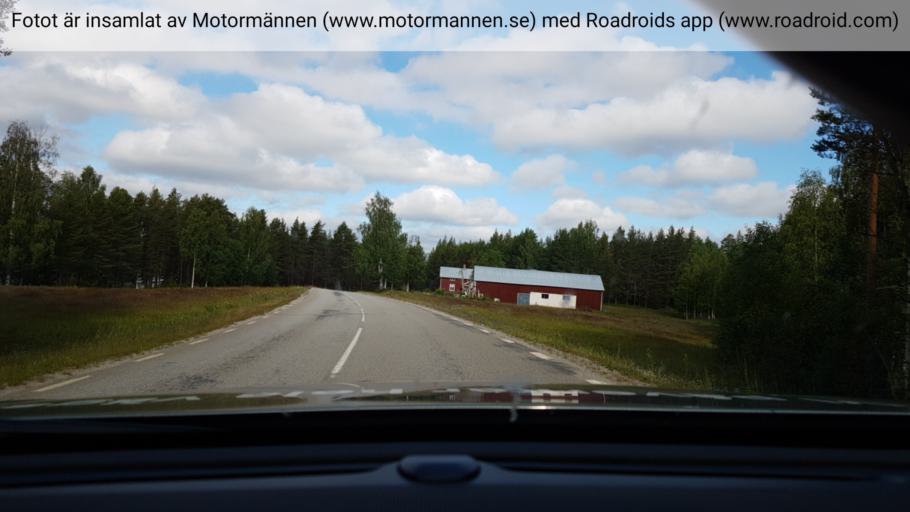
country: SE
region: Vaesterbotten
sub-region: Norsjo Kommun
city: Norsjoe
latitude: 64.7545
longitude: 19.0866
